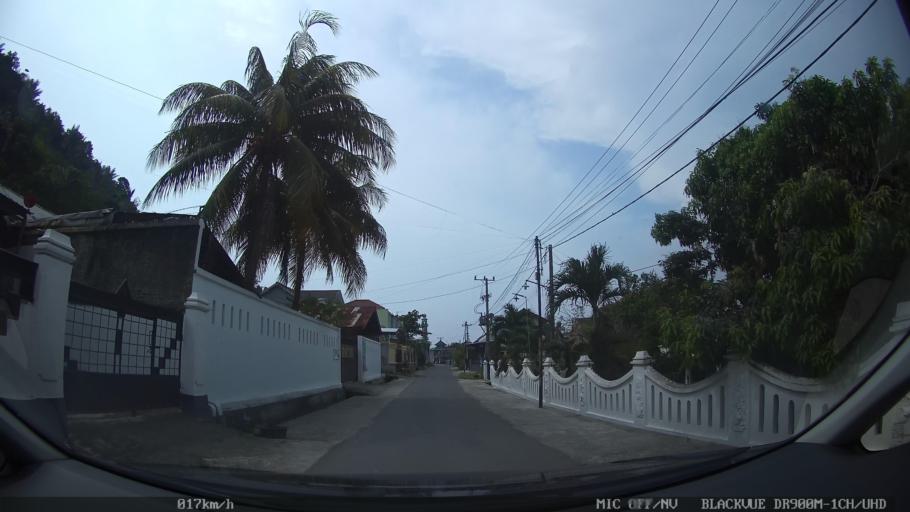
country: ID
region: Lampung
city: Bandarlampung
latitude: -5.4246
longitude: 105.2832
